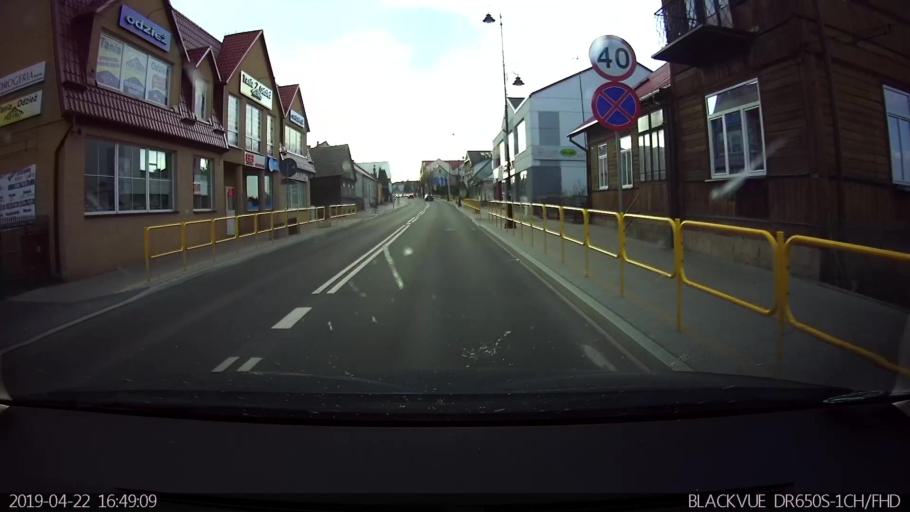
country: PL
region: Podlasie
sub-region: Powiat siemiatycki
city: Siemiatycze
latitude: 52.4273
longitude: 22.8667
